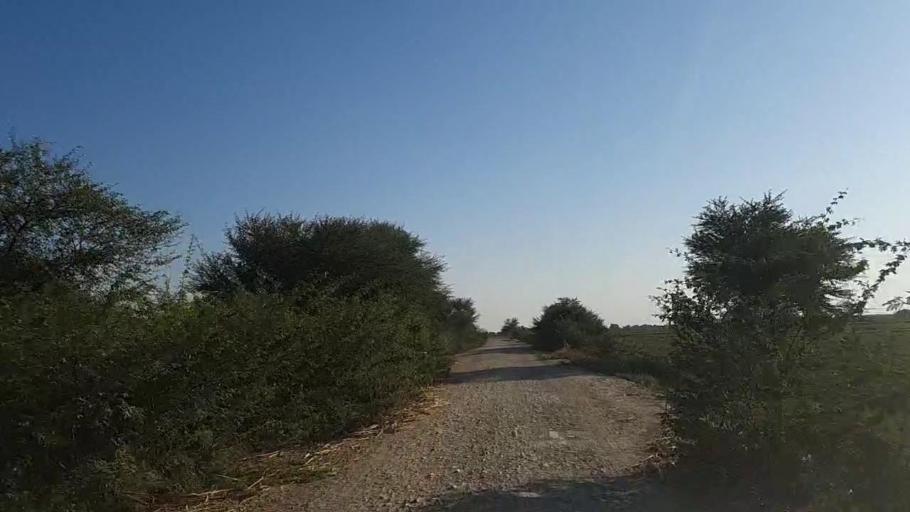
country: PK
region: Sindh
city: Naukot
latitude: 24.9622
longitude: 69.3881
